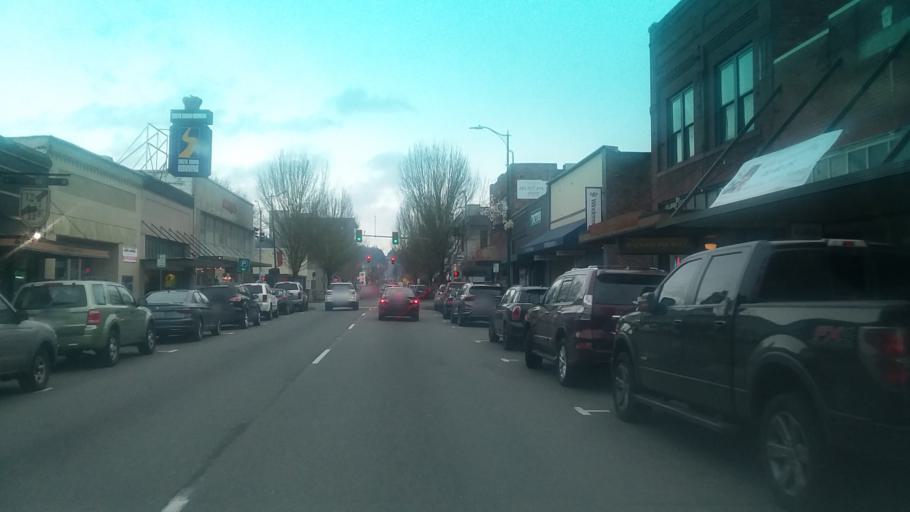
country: US
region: Washington
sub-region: Pierce County
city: Puyallup
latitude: 47.1916
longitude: -122.2938
